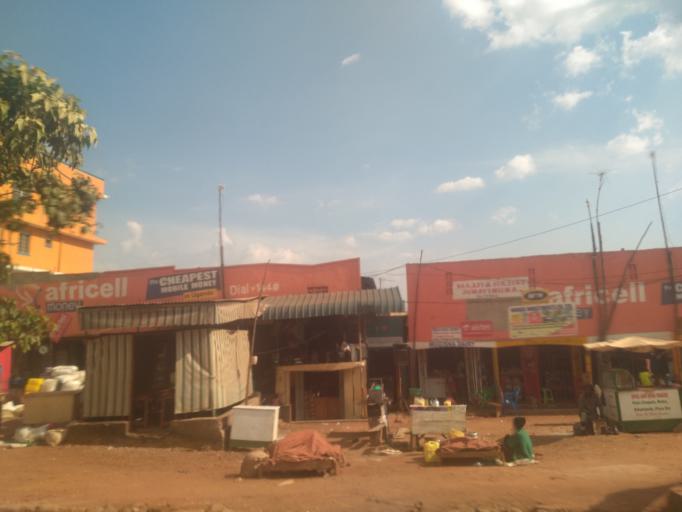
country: UG
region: Central Region
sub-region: Wakiso District
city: Kajansi
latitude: 0.2729
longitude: 32.4663
